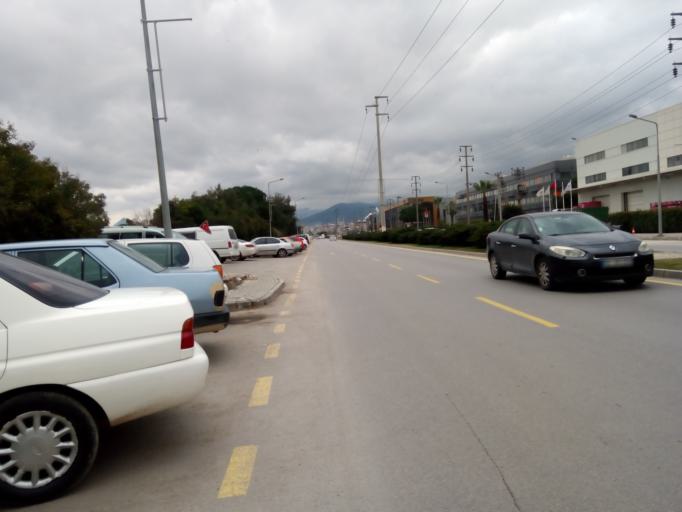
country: TR
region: Bursa
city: Niluefer
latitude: 40.2470
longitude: 28.9566
